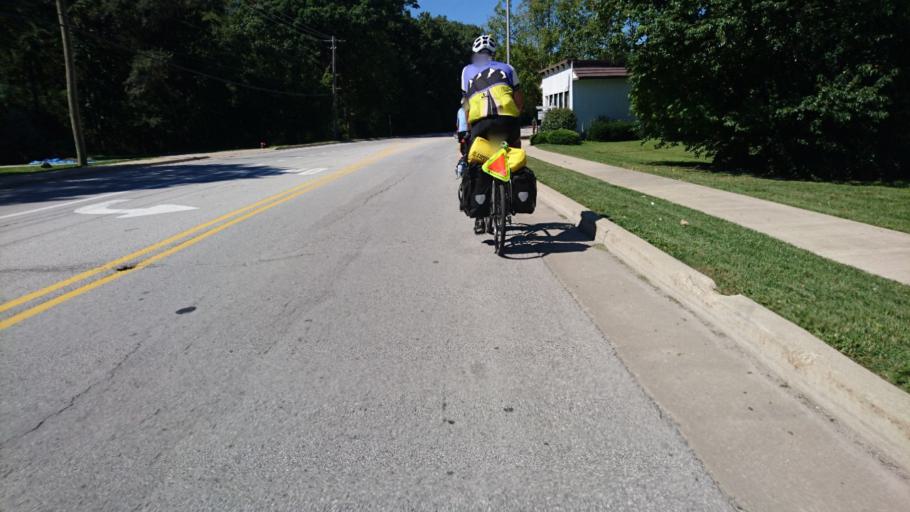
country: US
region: Illinois
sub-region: Cook County
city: Glenwood
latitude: 41.5451
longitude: -87.6161
